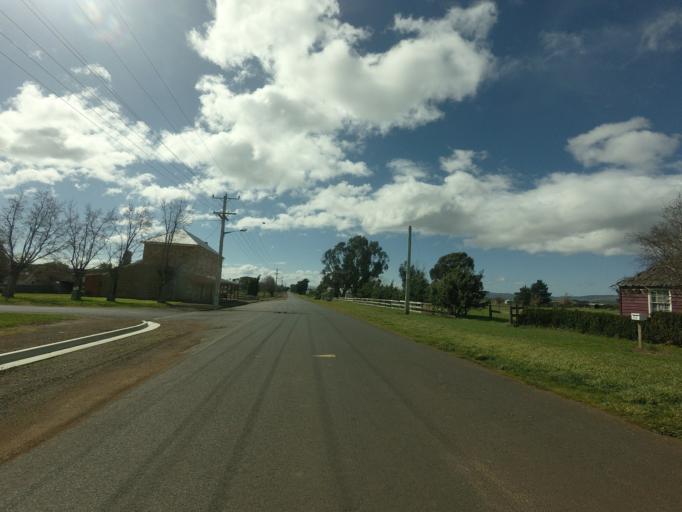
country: AU
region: Tasmania
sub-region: Northern Midlands
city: Evandale
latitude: -42.1420
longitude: 147.4222
